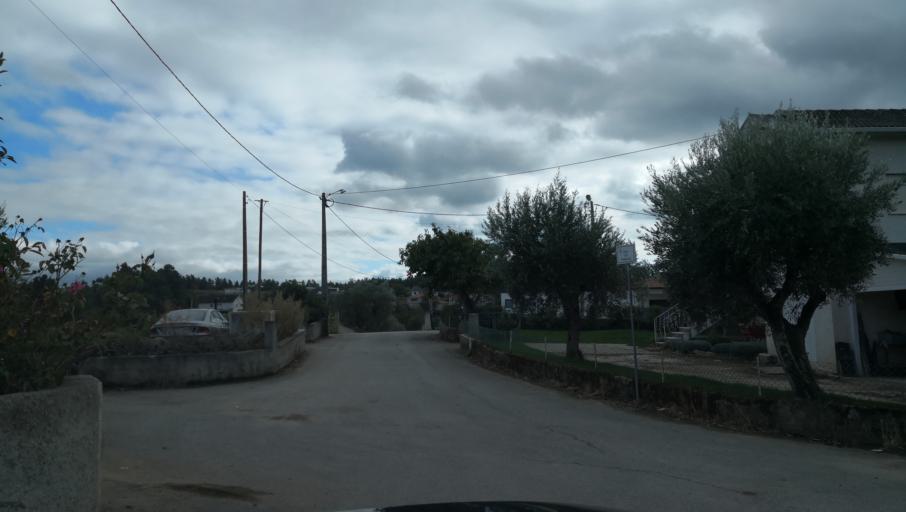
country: PT
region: Vila Real
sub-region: Vila Real
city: Vila Real
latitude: 41.2711
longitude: -7.7030
